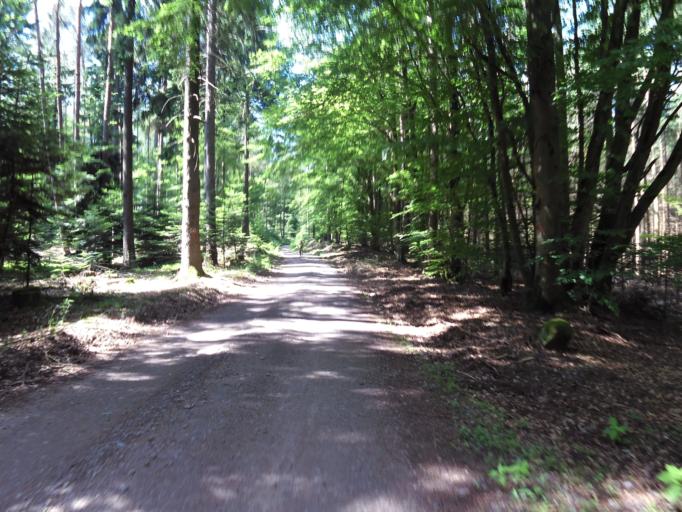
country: DE
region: Rheinland-Pfalz
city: Eusserthal
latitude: 49.2942
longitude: 7.9486
